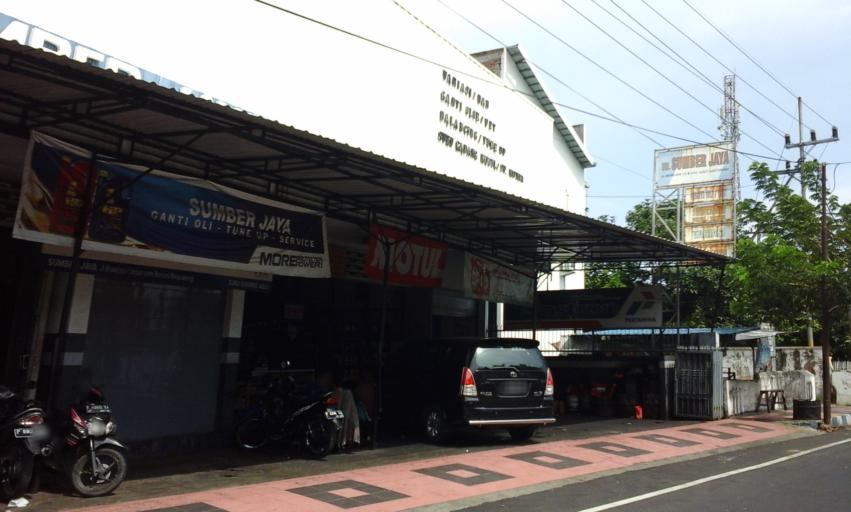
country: ID
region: East Java
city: Banyuwangi
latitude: -8.2355
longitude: 114.3578
